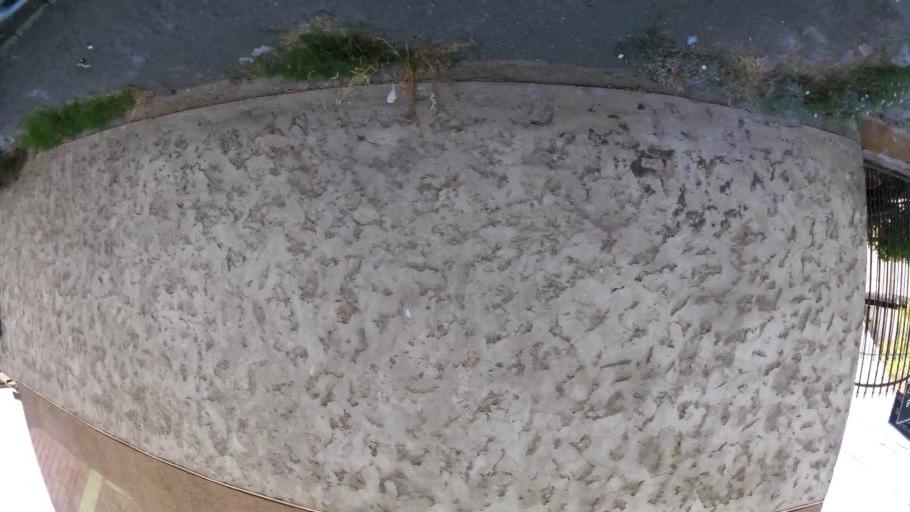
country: CL
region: Maule
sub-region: Provincia de Talca
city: Talca
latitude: -35.4132
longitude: -71.6448
